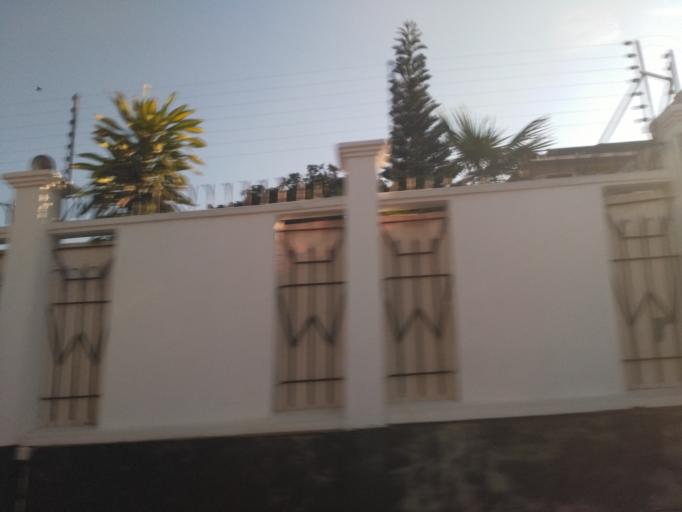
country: TZ
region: Dar es Salaam
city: Magomeni
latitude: -6.7616
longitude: 39.2556
